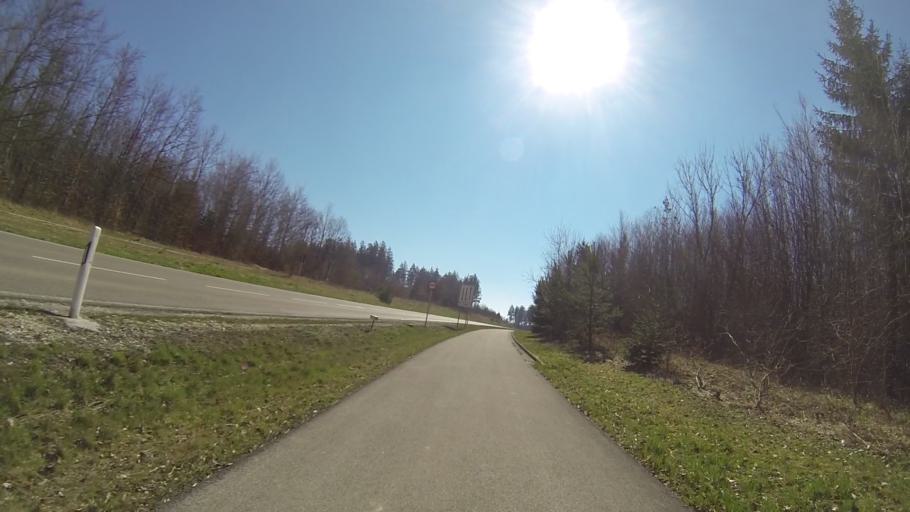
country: DE
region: Baden-Wuerttemberg
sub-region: Regierungsbezirk Stuttgart
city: Nattheim
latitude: 48.6680
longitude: 10.2546
